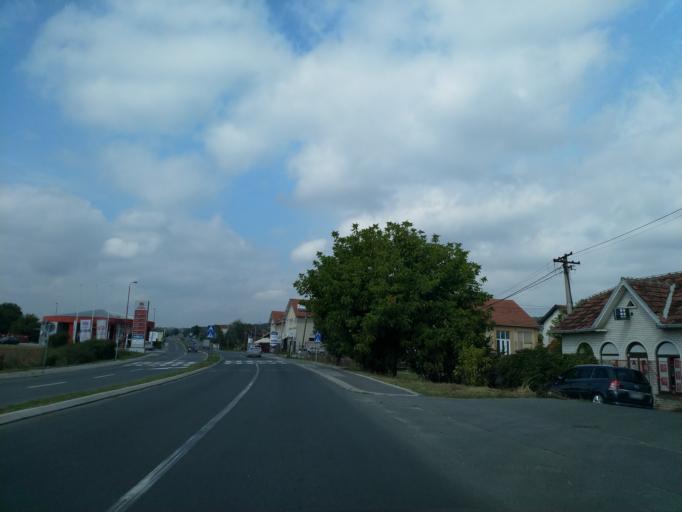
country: RS
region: Central Serbia
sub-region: Sumadijski Okrug
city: Kragujevac
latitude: 44.0433
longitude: 20.9093
